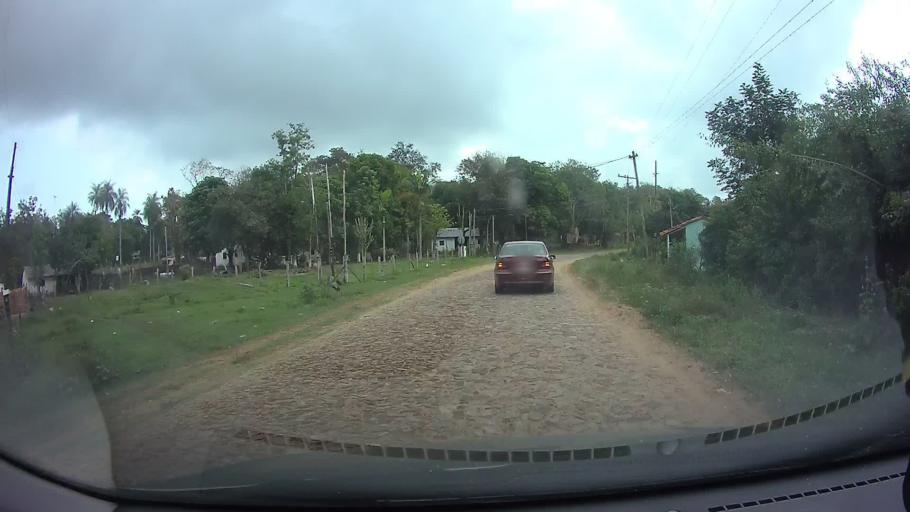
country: PY
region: Cordillera
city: Arroyos y Esteros
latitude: -25.0074
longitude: -57.1327
